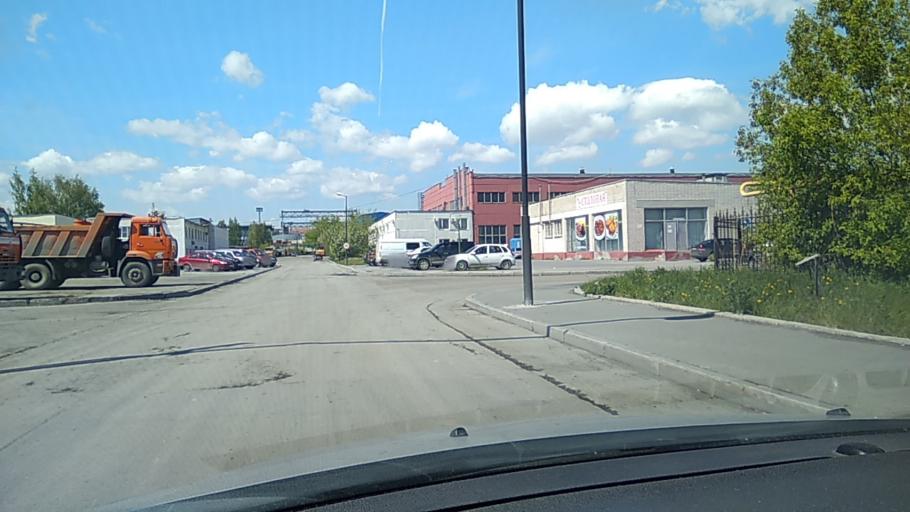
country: RU
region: Sverdlovsk
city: Istok
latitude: 56.7544
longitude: 60.7454
